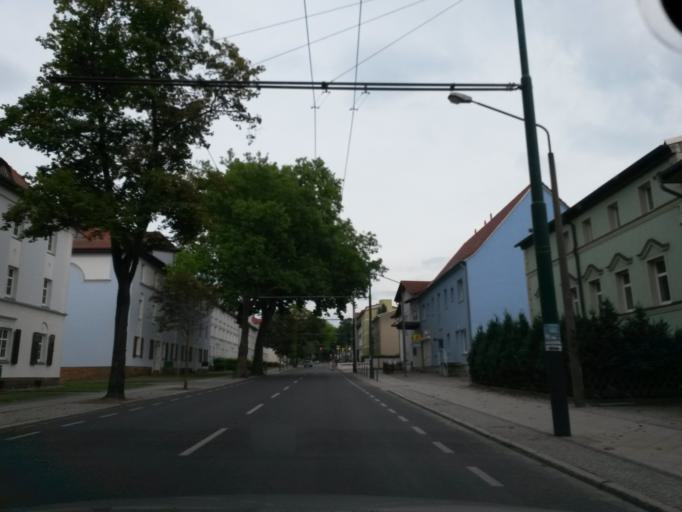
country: DE
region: Brandenburg
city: Eberswalde
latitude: 52.8289
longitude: 13.8335
